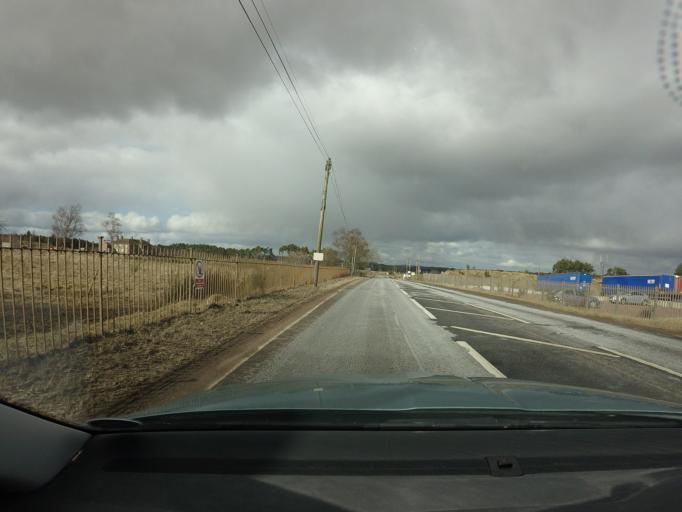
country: GB
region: Scotland
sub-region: South Lanarkshire
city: Lanark
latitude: 55.6615
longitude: -3.7276
